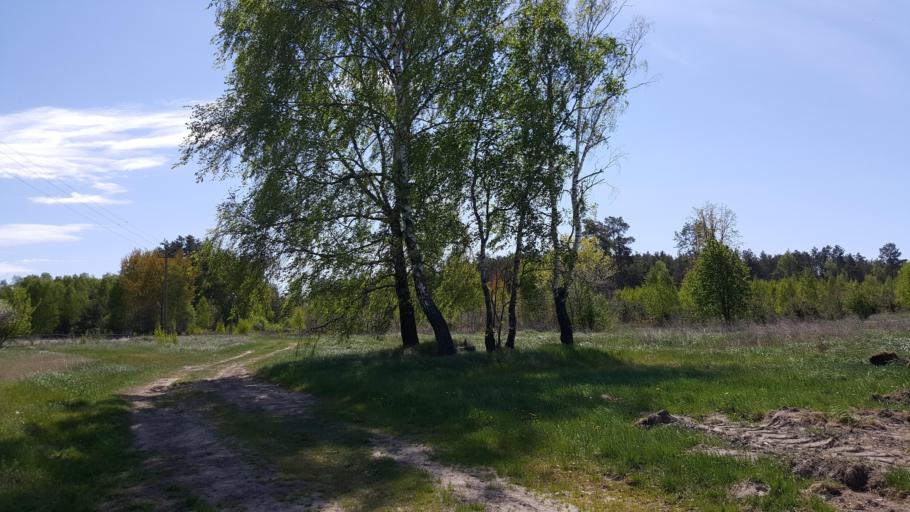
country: BY
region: Brest
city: Zhabinka
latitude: 52.3615
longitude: 24.0560
